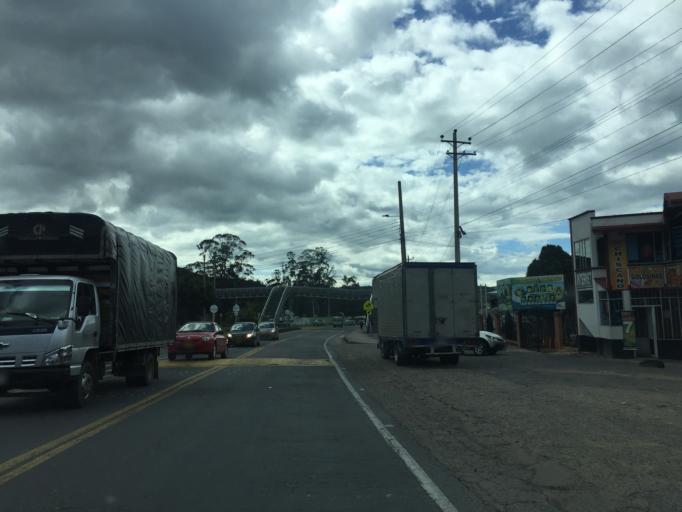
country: CO
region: Boyaca
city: Arcabuco
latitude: 5.7570
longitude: -73.4394
